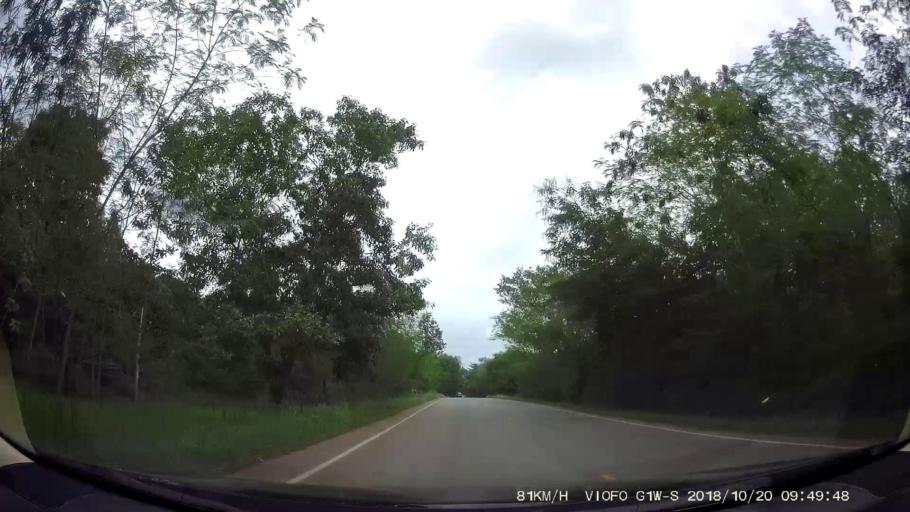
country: TH
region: Chaiyaphum
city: Khon San
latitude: 16.5238
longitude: 101.9040
